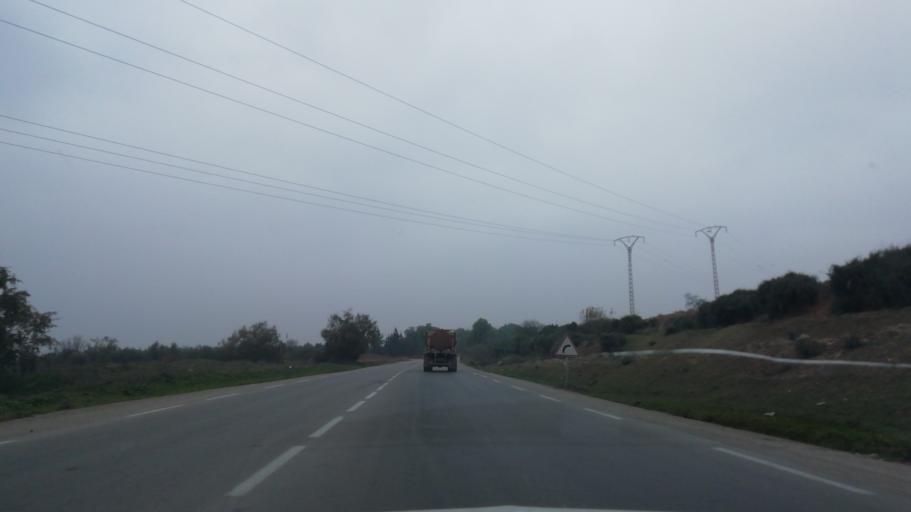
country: DZ
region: Mascara
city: Mascara
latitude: 35.3814
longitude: 0.1591
